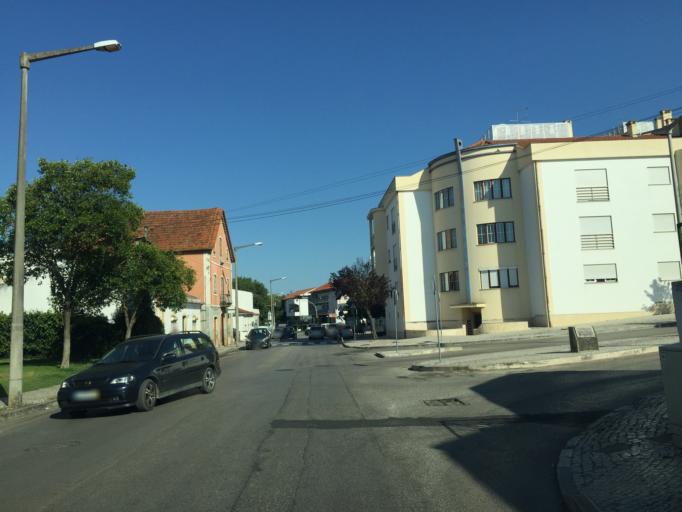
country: PT
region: Santarem
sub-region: Tomar
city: Tomar
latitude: 39.6036
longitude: -8.4012
